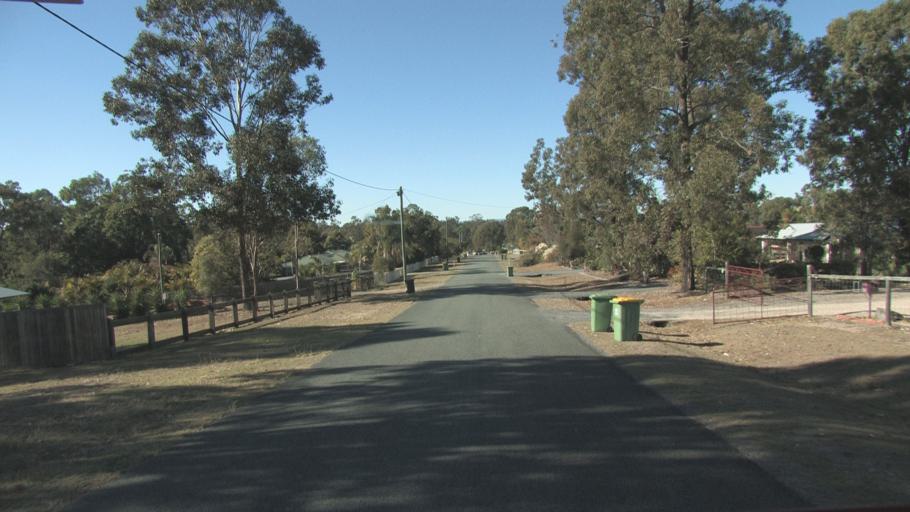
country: AU
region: Queensland
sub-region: Logan
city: North Maclean
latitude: -27.7405
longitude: 152.9657
